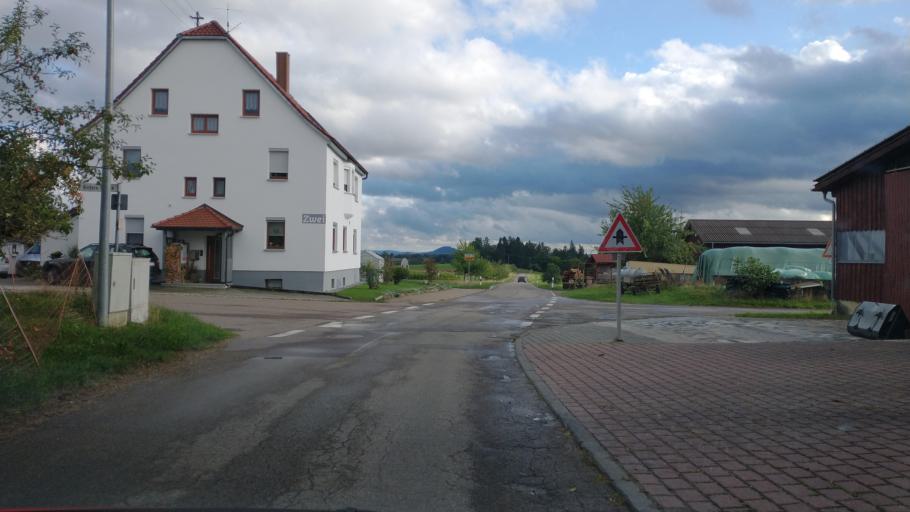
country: DE
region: Baden-Wuerttemberg
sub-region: Regierungsbezirk Stuttgart
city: Alfdorf
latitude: 48.8543
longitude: 9.6931
